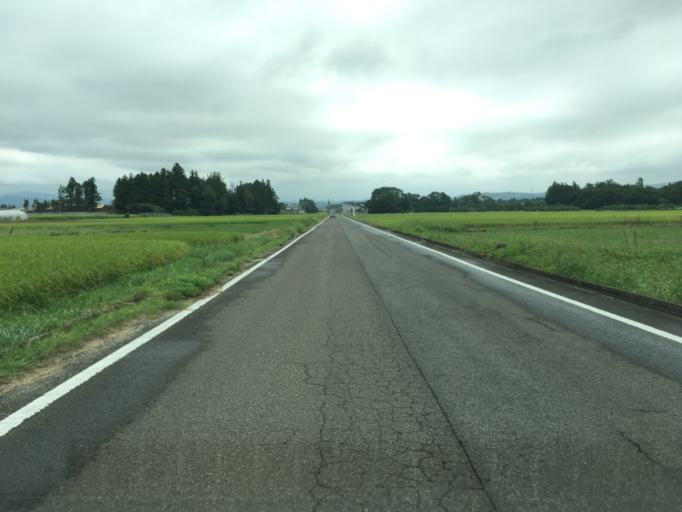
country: JP
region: Fukushima
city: Fukushima-shi
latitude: 37.7650
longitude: 140.3902
